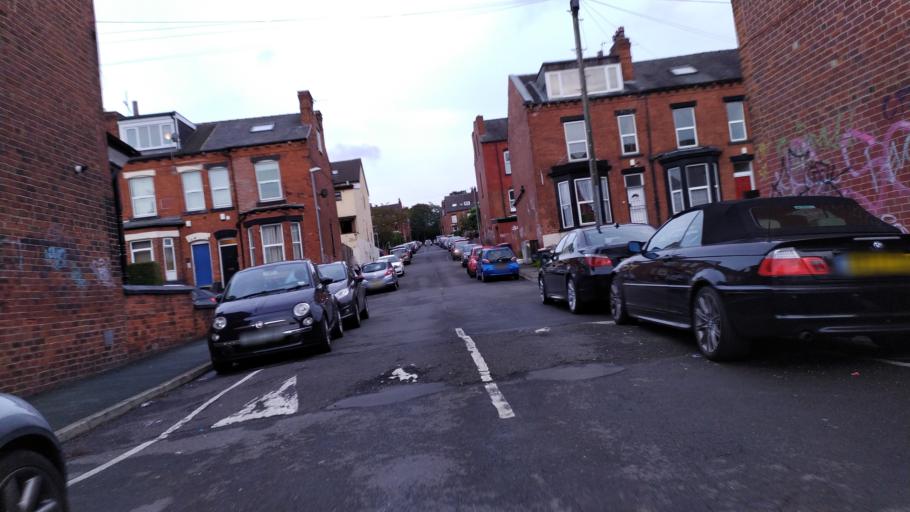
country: GB
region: England
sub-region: City and Borough of Leeds
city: Leeds
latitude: 53.8113
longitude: -1.5689
